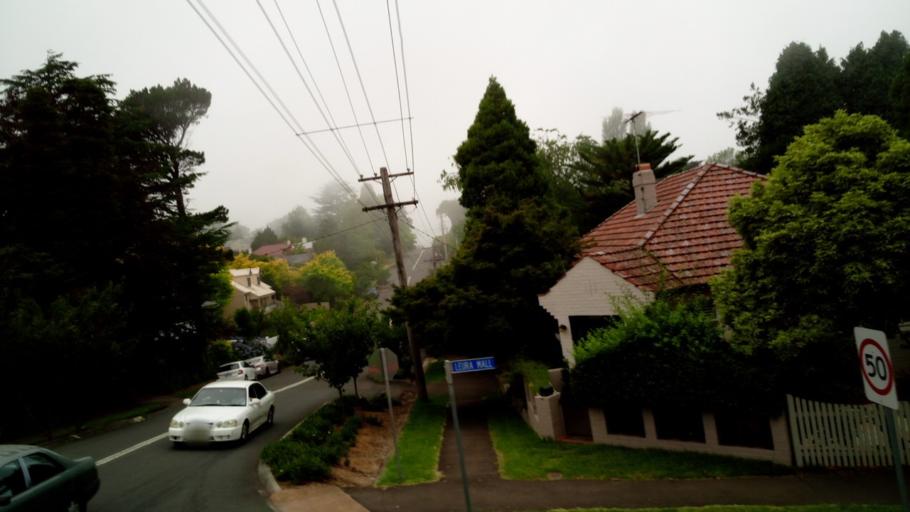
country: AU
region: New South Wales
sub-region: Blue Mountains Municipality
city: Leura
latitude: -33.7157
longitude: 150.3297
